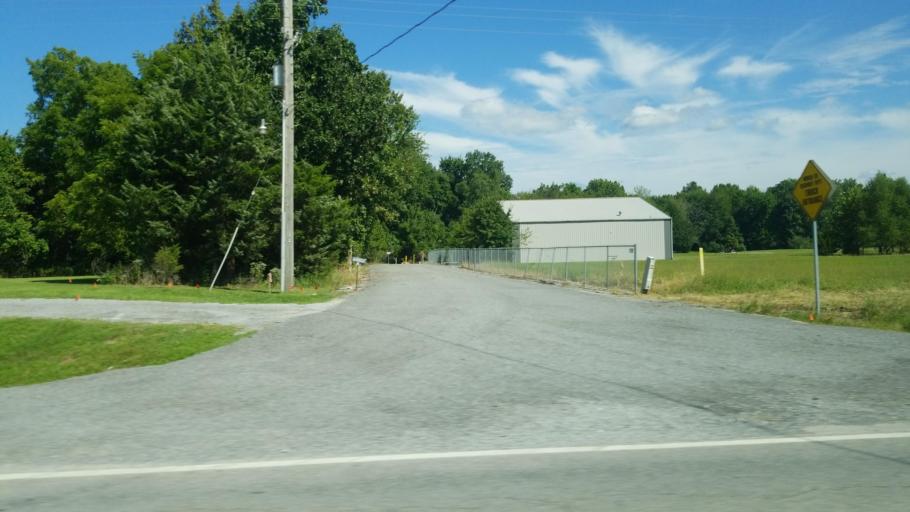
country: US
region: Illinois
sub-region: Williamson County
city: Marion
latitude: 37.7502
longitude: -88.9327
